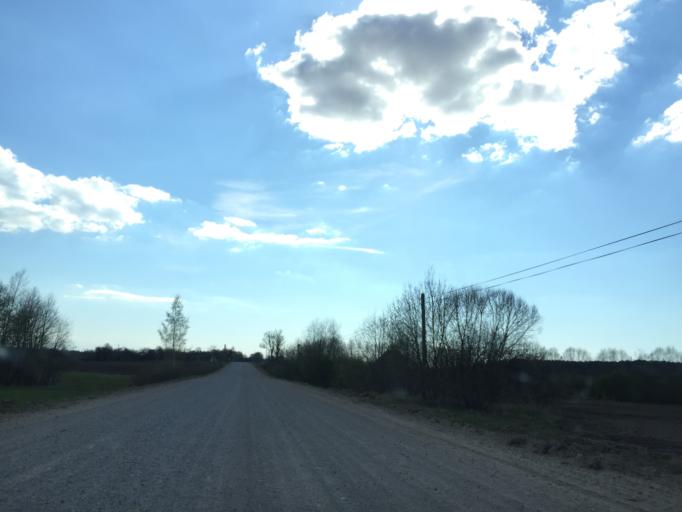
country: LV
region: Saulkrastu
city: Saulkrasti
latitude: 57.3426
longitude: 24.5299
